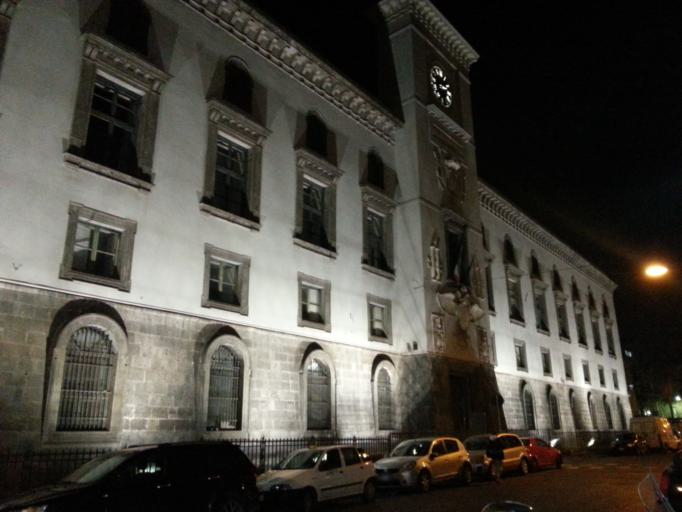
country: IT
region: Campania
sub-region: Provincia di Napoli
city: Napoli
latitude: 40.8532
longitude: 14.2637
